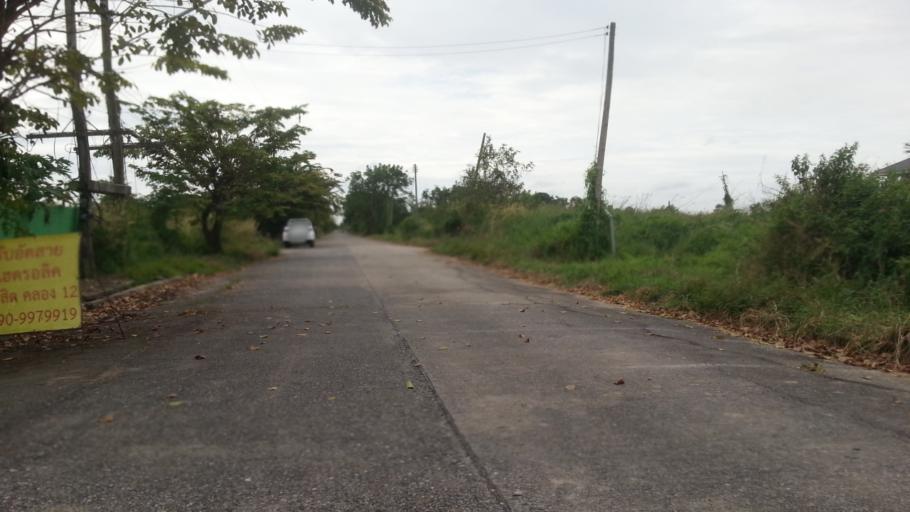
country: TH
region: Pathum Thani
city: Nong Suea
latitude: 14.0659
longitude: 100.8785
